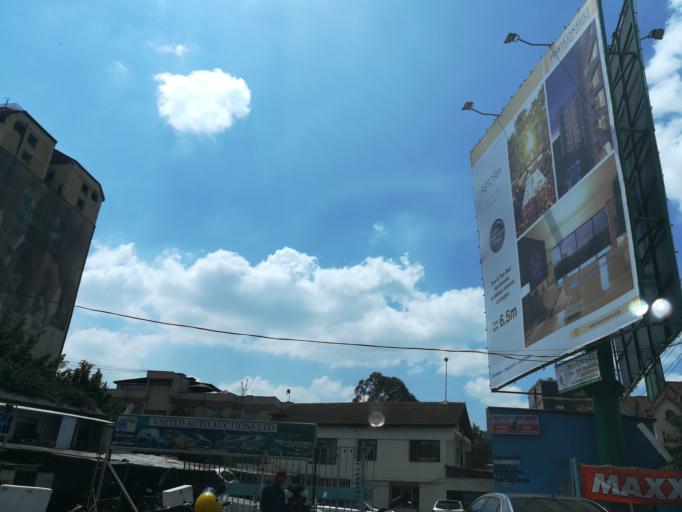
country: KE
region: Nairobi Area
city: Nairobi
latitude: -1.2943
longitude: 36.7876
